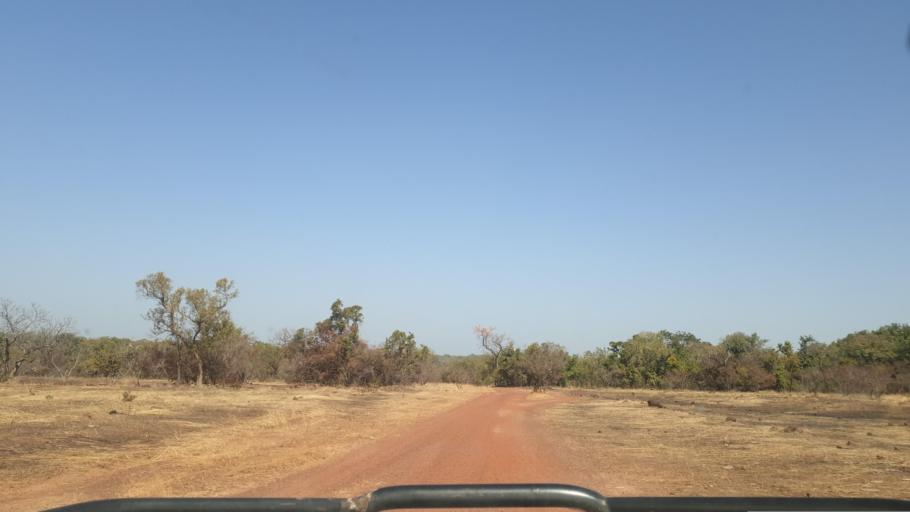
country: ML
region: Koulikoro
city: Dioila
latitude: 11.9202
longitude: -6.9838
